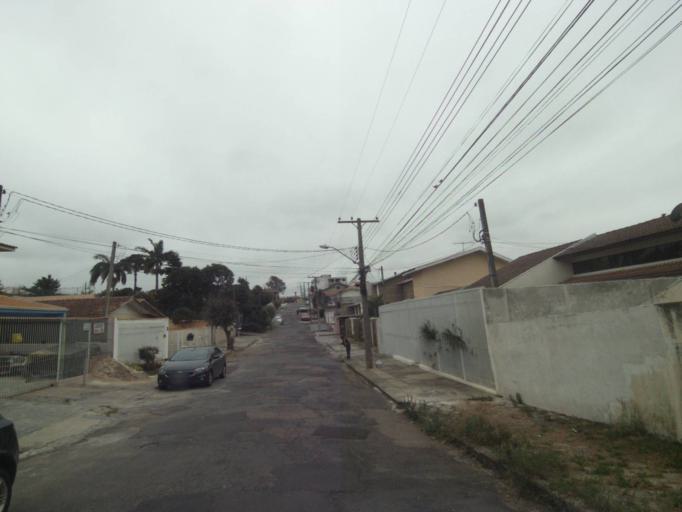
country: BR
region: Parana
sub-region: Pinhais
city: Pinhais
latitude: -25.4743
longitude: -49.2374
